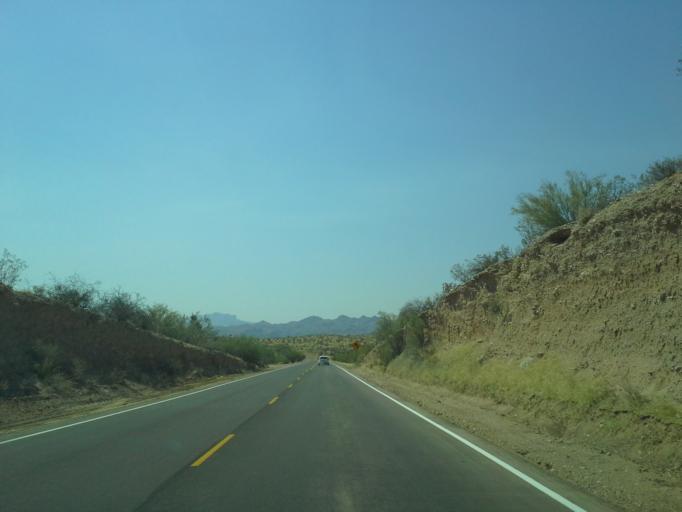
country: US
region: Arizona
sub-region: Maricopa County
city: Rio Verde
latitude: 33.6160
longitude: -111.5543
